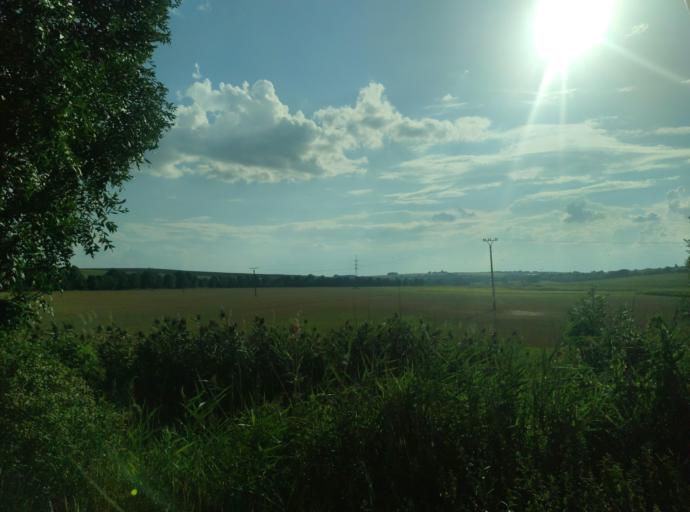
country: CZ
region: South Moravian
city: Vinicne Sumice
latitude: 49.1828
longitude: 16.8456
